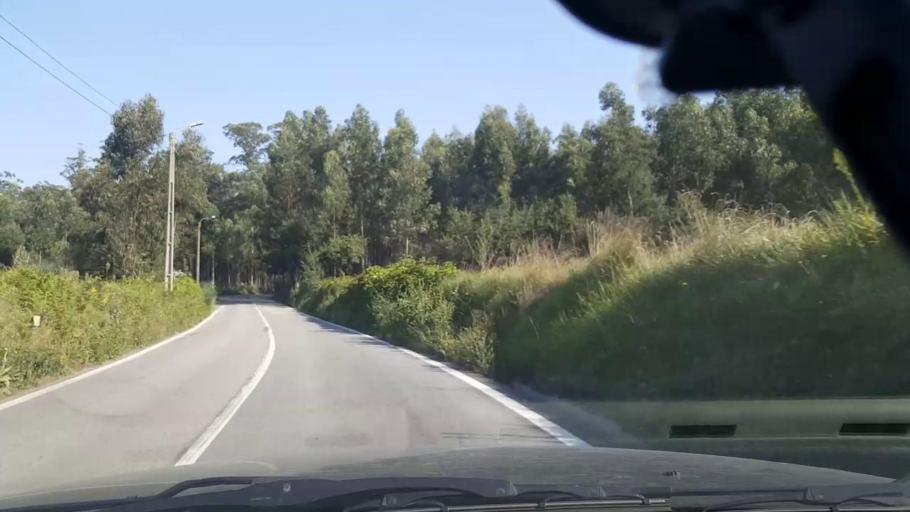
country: PT
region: Porto
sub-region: Maia
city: Gemunde
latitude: 41.2913
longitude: -8.6827
